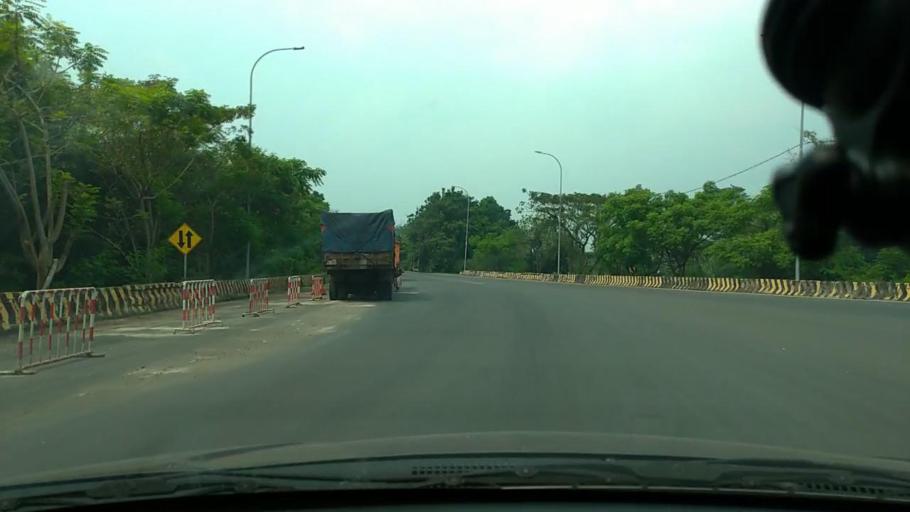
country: ID
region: Banten
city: Serang
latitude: -6.0908
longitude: 106.1366
